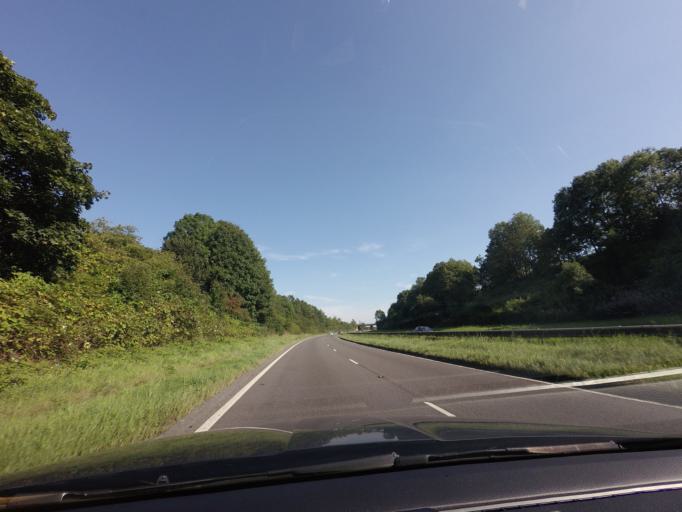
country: GB
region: England
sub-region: Derbyshire
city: Chesterfield
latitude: 53.2251
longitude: -1.4041
